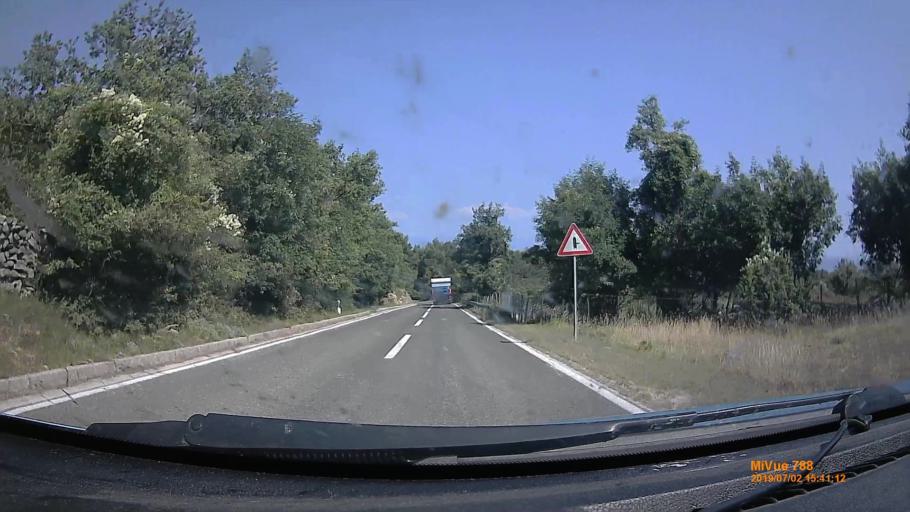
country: HR
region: Primorsko-Goranska
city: Cres
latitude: 44.9610
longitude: 14.4393
